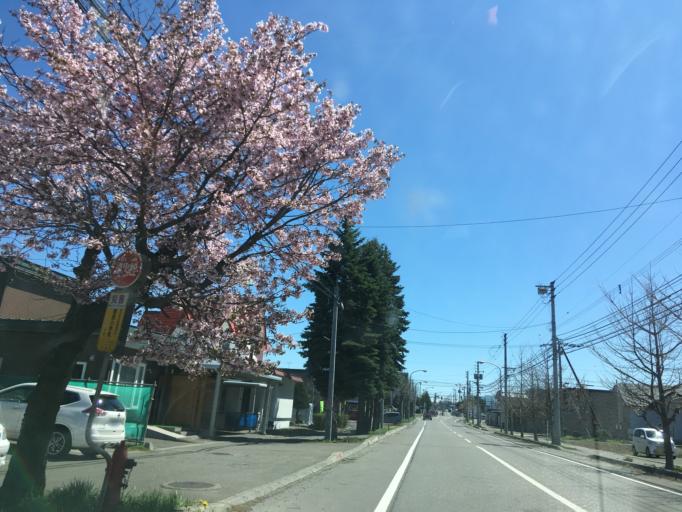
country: JP
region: Hokkaido
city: Obihiro
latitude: 42.9215
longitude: 143.1714
